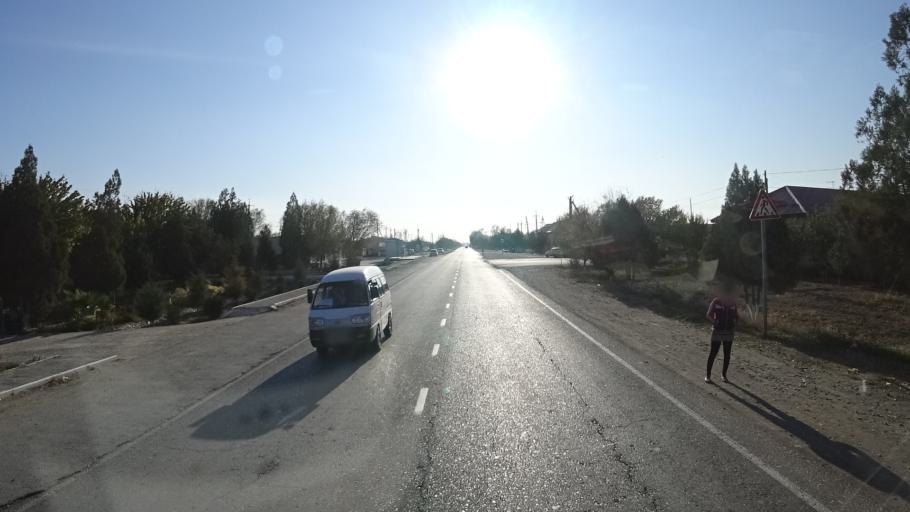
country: UZ
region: Navoiy
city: Beshrabot
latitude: 40.1870
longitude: 65.3590
